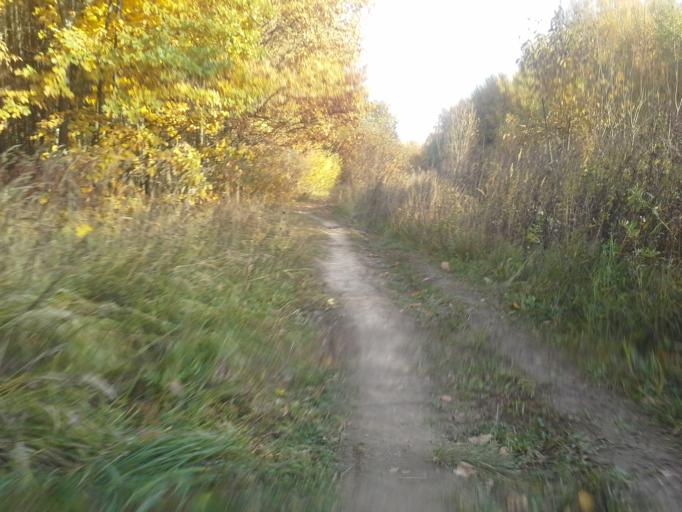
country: RU
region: Moskovskaya
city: Kommunarka
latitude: 55.5554
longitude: 37.5286
